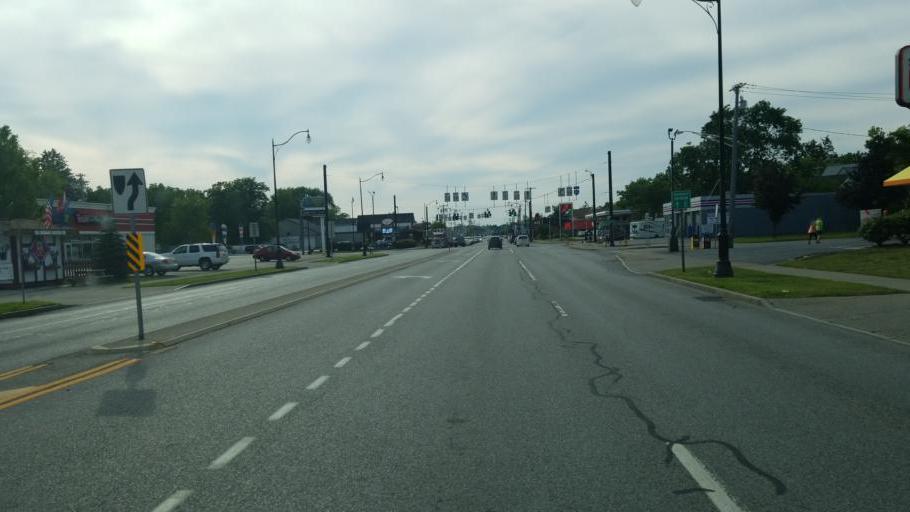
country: US
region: New York
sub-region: Genesee County
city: Batavia
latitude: 42.9995
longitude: -78.1908
